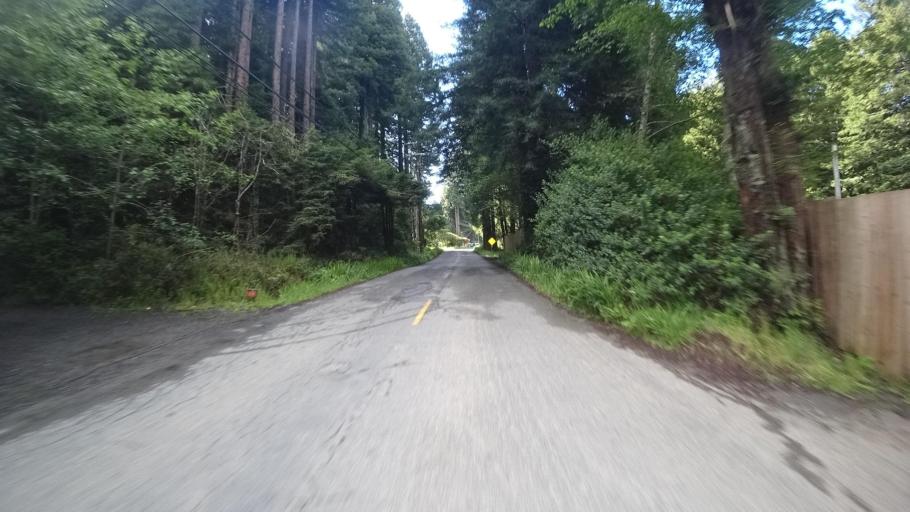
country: US
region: California
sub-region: Humboldt County
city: Westhaven-Moonstone
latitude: 41.0395
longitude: -124.1084
